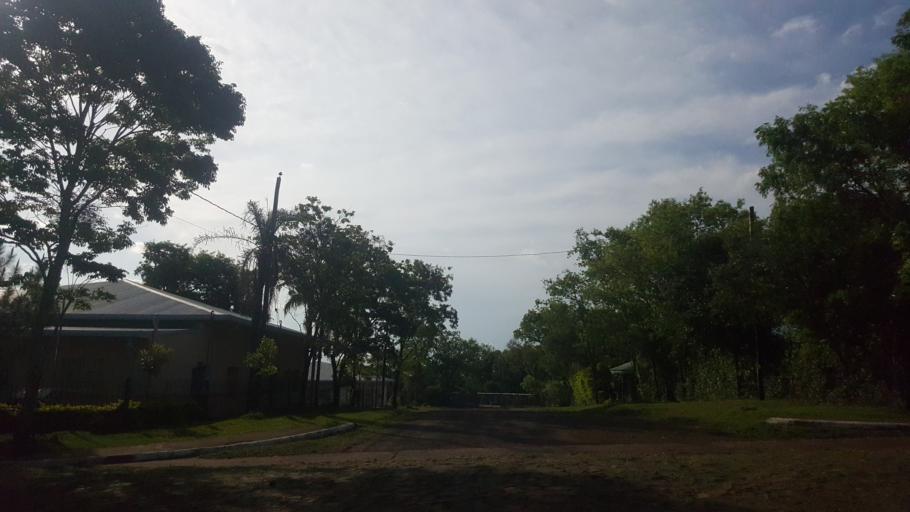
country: AR
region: Misiones
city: Cerro Cora
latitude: -27.5610
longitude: -55.7062
